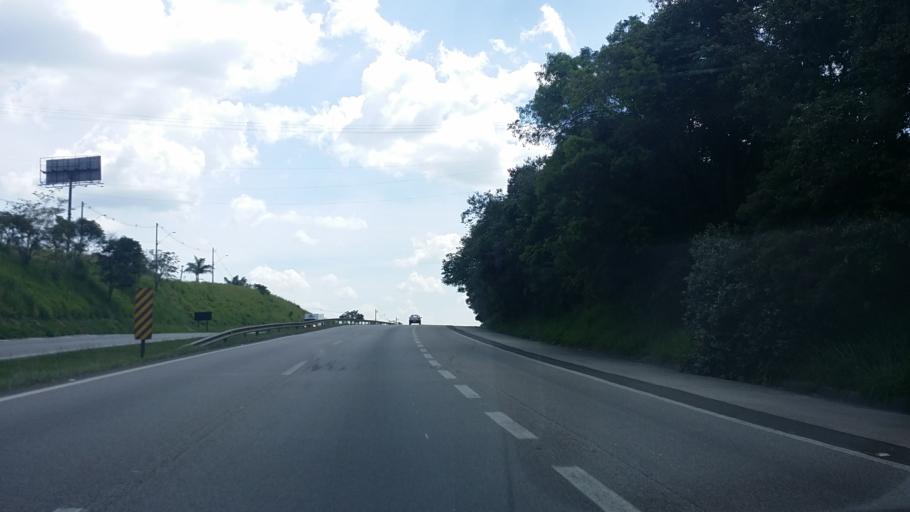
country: BR
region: Sao Paulo
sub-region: Itupeva
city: Itupeva
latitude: -23.1980
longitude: -46.9974
